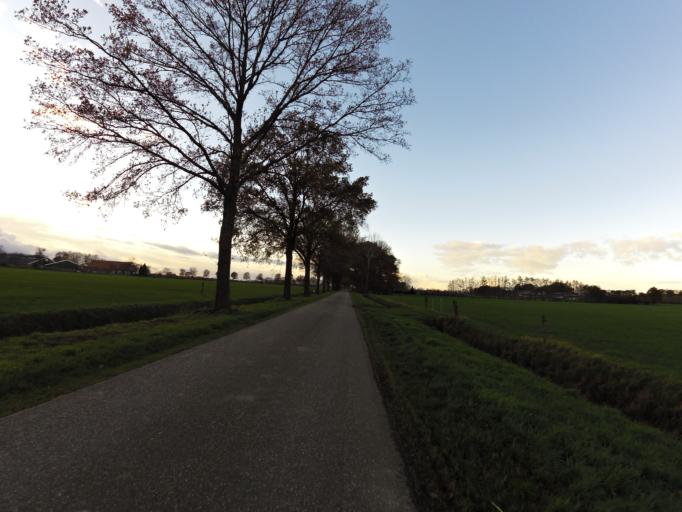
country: NL
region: Gelderland
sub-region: Oude IJsselstreek
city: Gendringen
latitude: 51.8542
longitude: 6.3627
